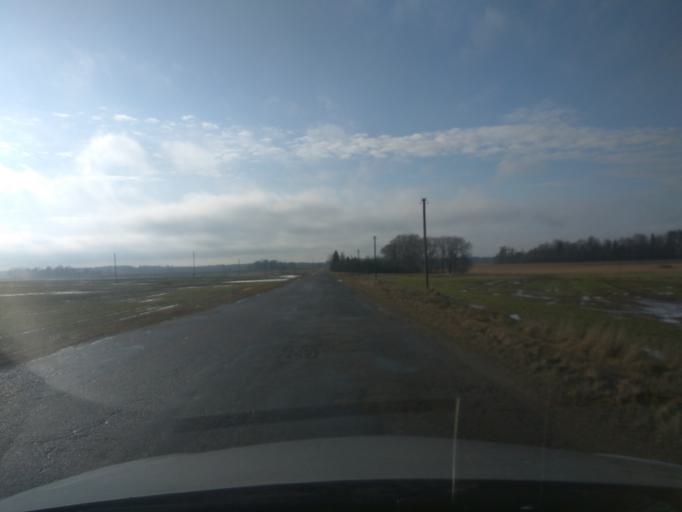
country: LV
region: Saldus Rajons
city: Saldus
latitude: 56.8264
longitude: 22.3892
